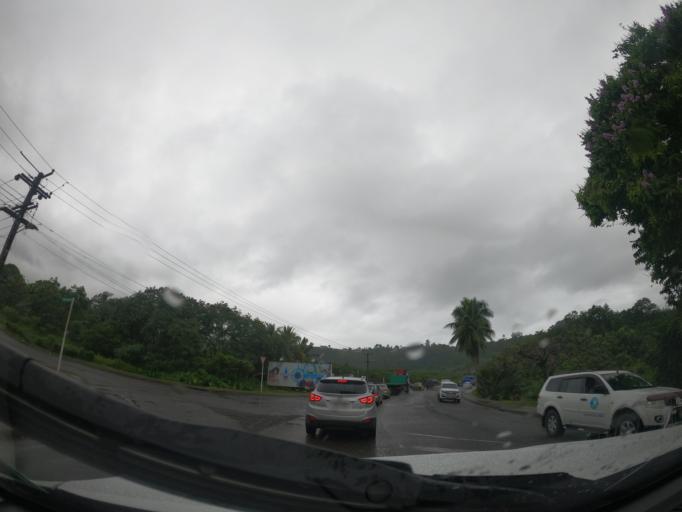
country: FJ
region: Central
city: Suva
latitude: -18.1129
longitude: 178.4295
